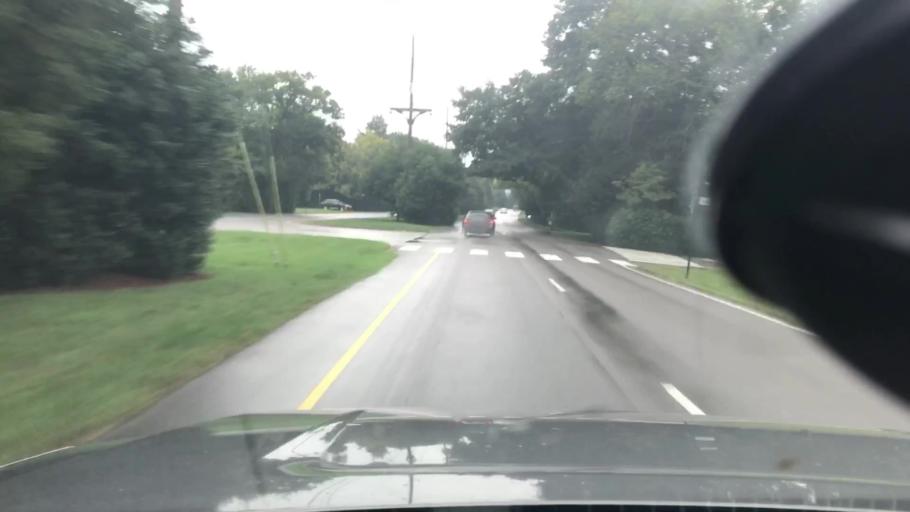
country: US
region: Tennessee
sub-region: Davidson County
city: Belle Meade
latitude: 36.1025
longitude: -86.8570
